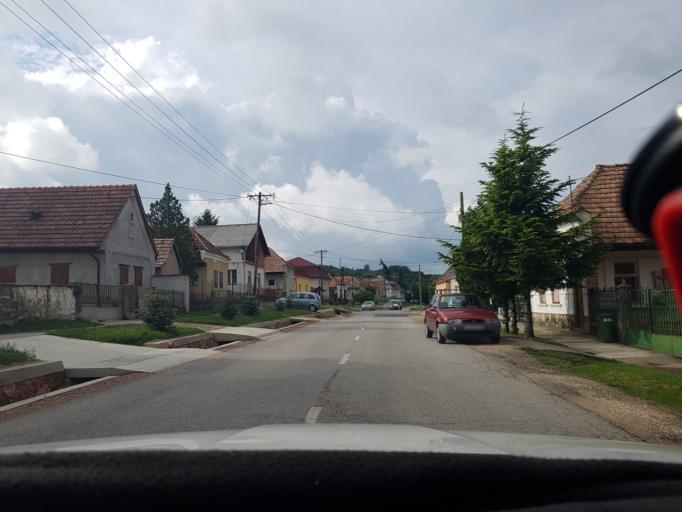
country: HU
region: Komarom-Esztergom
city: Neszmely
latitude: 47.7056
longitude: 18.3814
